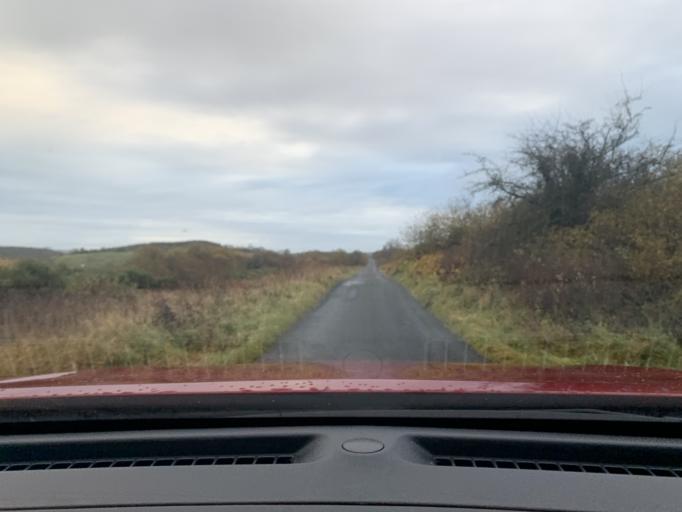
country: IE
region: Connaught
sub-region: Sligo
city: Ballymote
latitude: 54.0168
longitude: -8.5147
